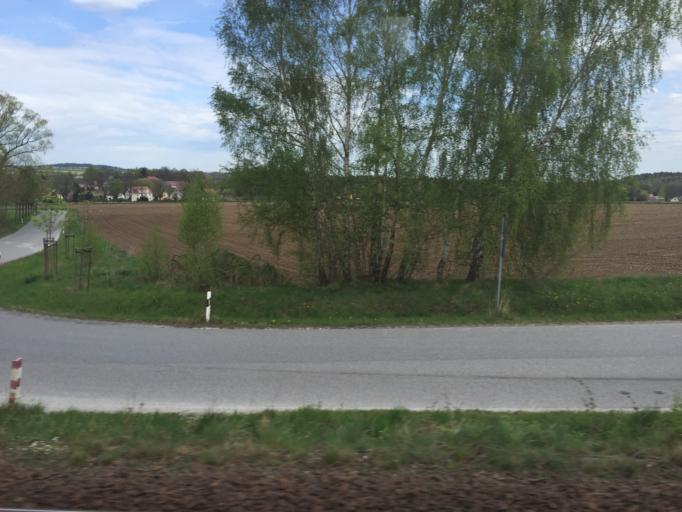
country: DE
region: Saxony
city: Demitz-Thumitz
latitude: 51.1382
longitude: 14.2550
